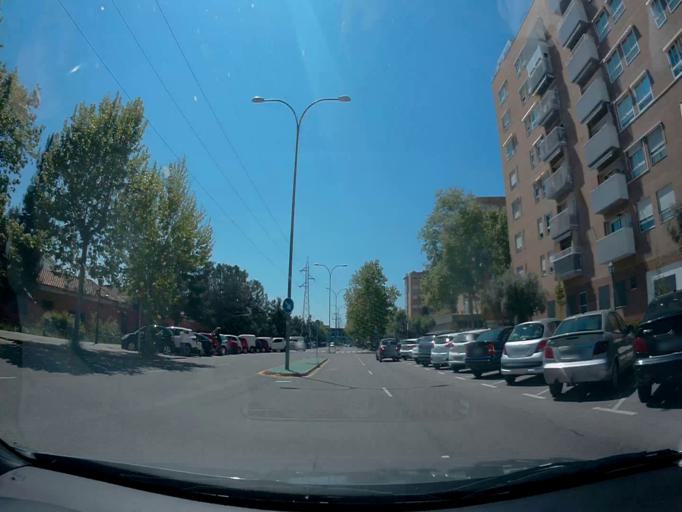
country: ES
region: Madrid
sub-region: Provincia de Madrid
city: Alcorcon
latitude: 40.3459
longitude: -3.8066
